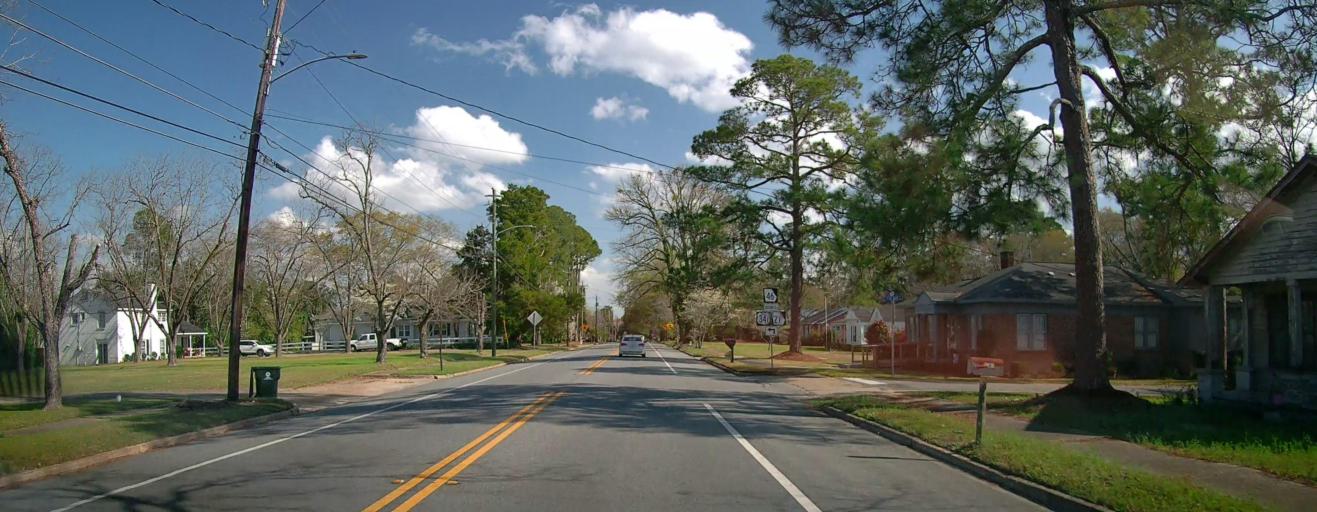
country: US
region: Georgia
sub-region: Dodge County
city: Eastman
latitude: 32.1957
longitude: -83.1848
